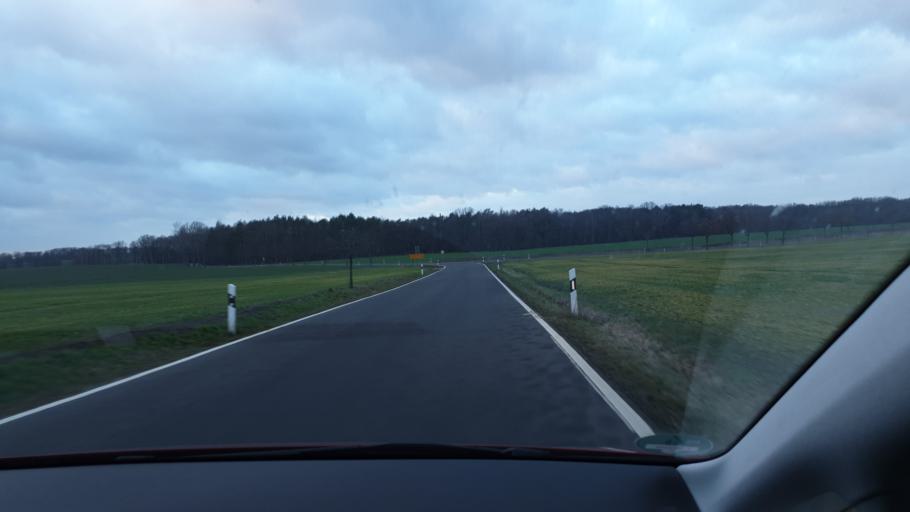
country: DE
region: Saxony
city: Falkenhain
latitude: 51.4527
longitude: 12.8580
